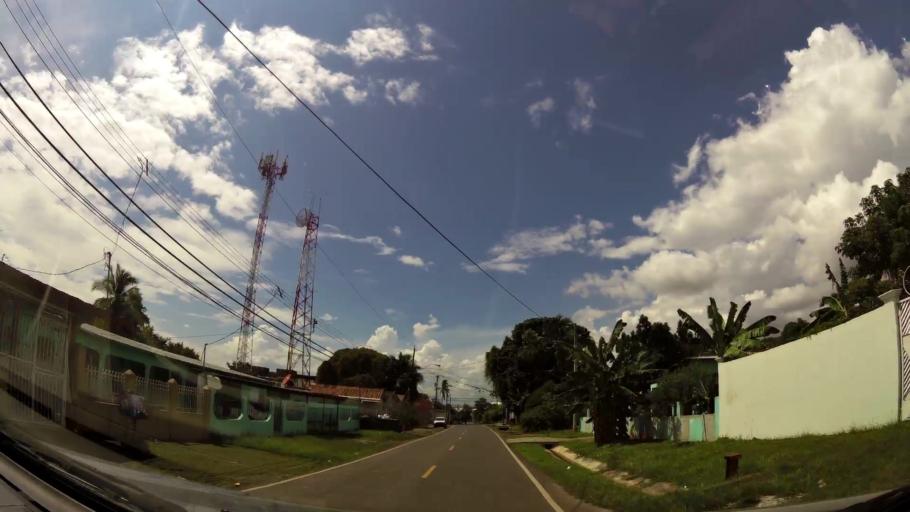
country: PA
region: Panama
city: Vista Alegre
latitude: 8.9261
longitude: -79.6989
